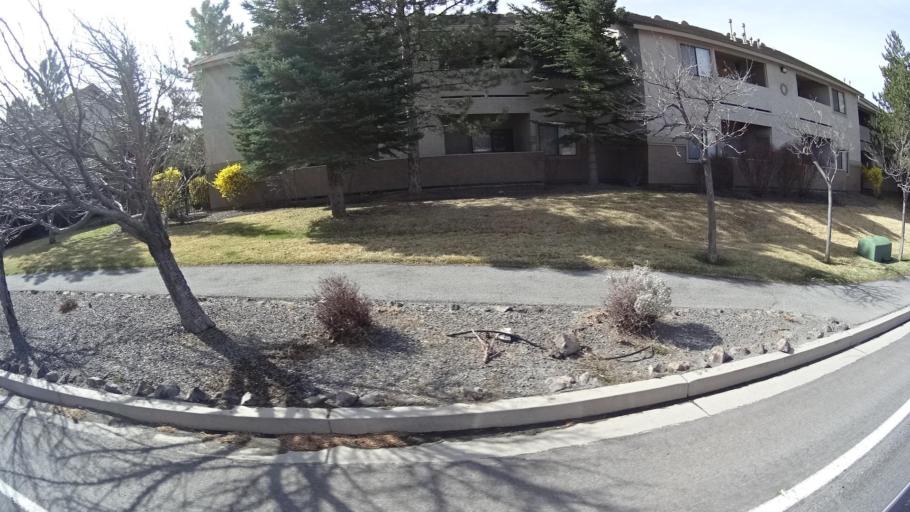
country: US
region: Nevada
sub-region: Washoe County
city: Mogul
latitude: 39.5190
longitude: -119.8923
